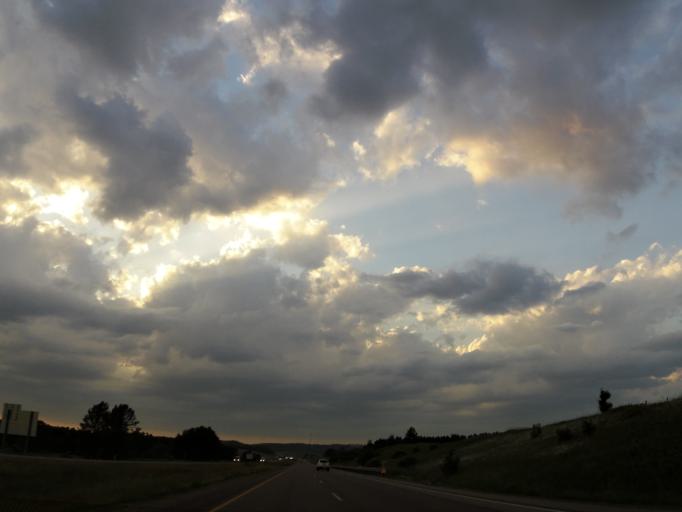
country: US
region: Wisconsin
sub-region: Trempealeau County
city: Osseo
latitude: 44.5833
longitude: -91.2080
